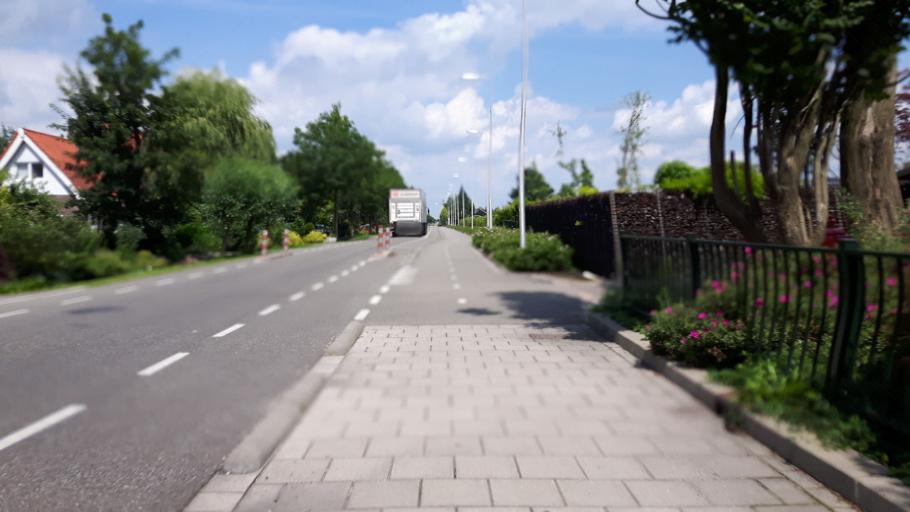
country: NL
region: South Holland
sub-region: Gemeente Boskoop
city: Boskoop
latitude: 52.0854
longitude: 4.6822
